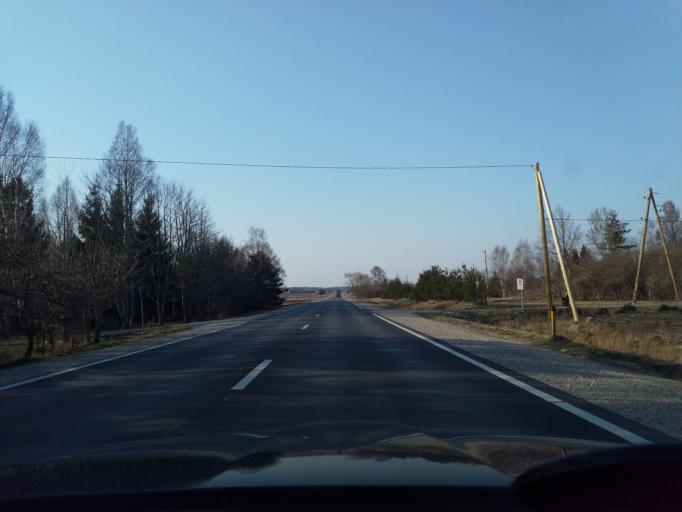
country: LV
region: Nica
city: Nica
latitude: 56.3856
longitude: 21.0013
